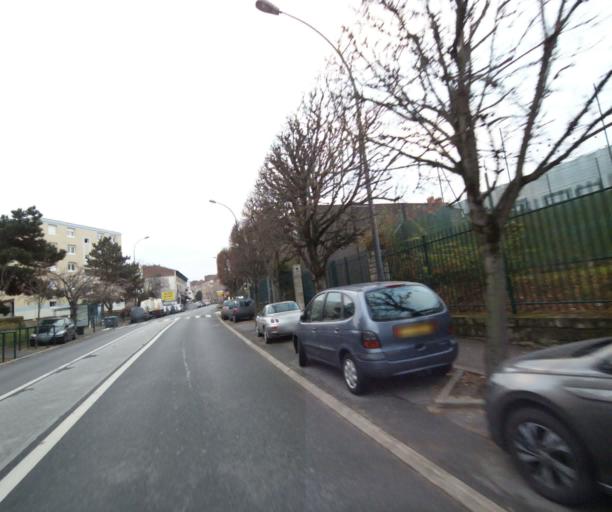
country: FR
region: Ile-de-France
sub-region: Departement des Hauts-de-Seine
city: Rueil-Malmaison
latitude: 48.8664
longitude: 2.2015
